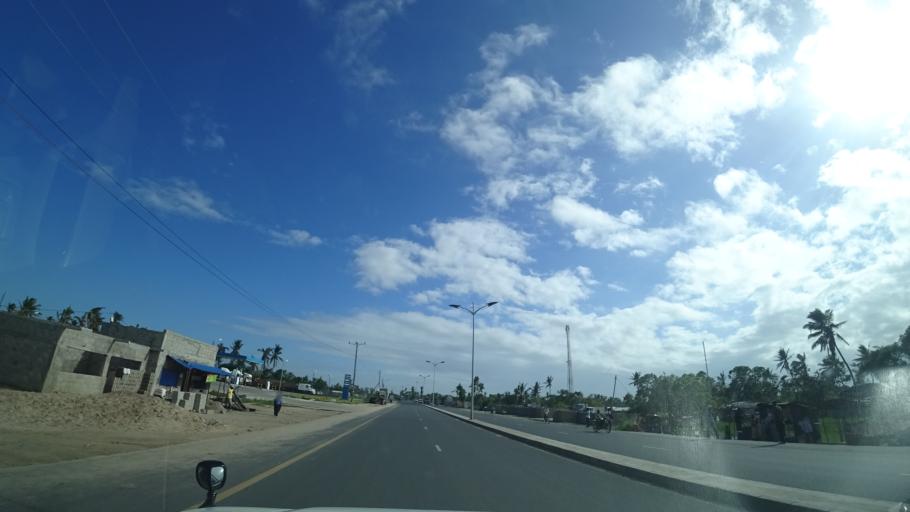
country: MZ
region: Sofala
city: Beira
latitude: -19.7542
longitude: 34.8767
